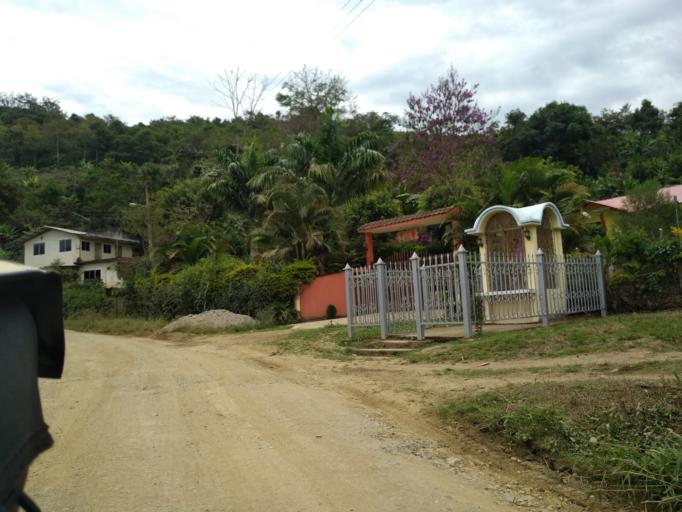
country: PE
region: Cajamarca
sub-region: Provincia de San Ignacio
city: Namballe
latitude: -4.8400
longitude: -79.1254
